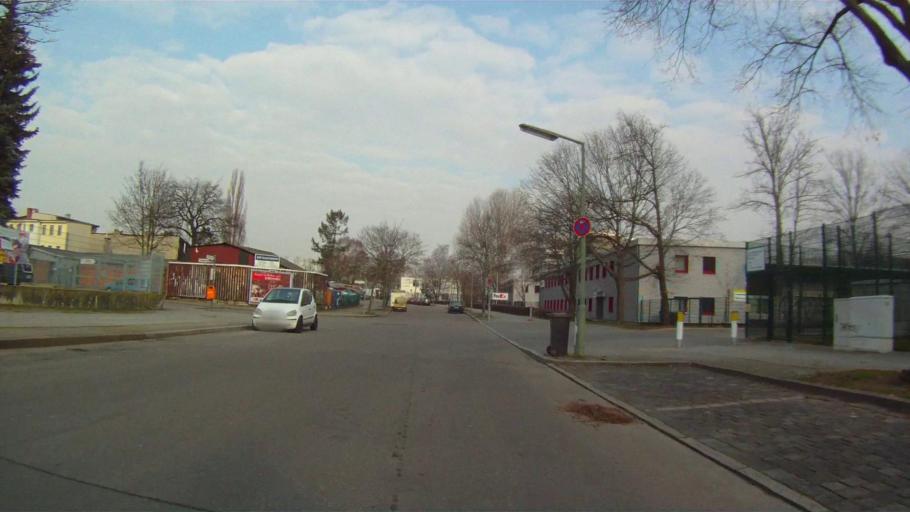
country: DE
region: Berlin
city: Britz
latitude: 52.4561
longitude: 13.4532
